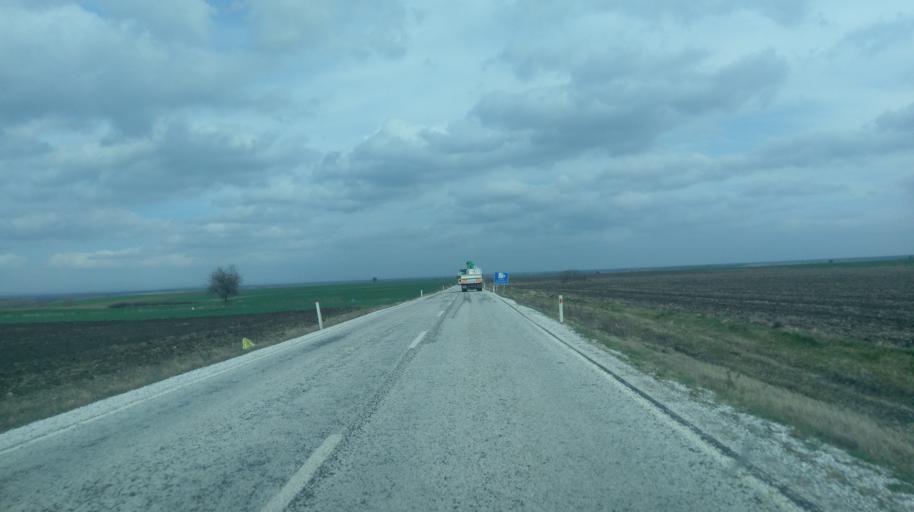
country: TR
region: Edirne
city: Haskoy
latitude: 41.6537
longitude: 26.9021
